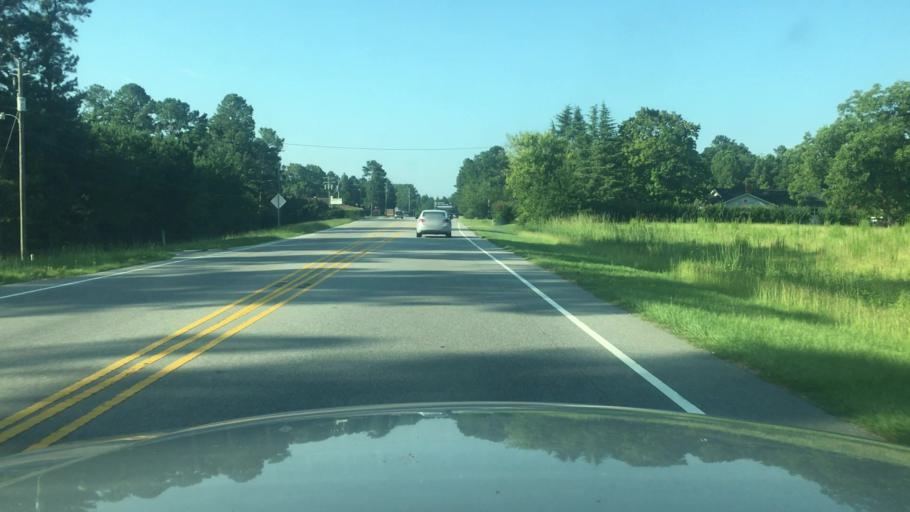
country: US
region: North Carolina
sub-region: Cumberland County
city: Eastover
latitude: 35.1865
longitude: -78.8524
